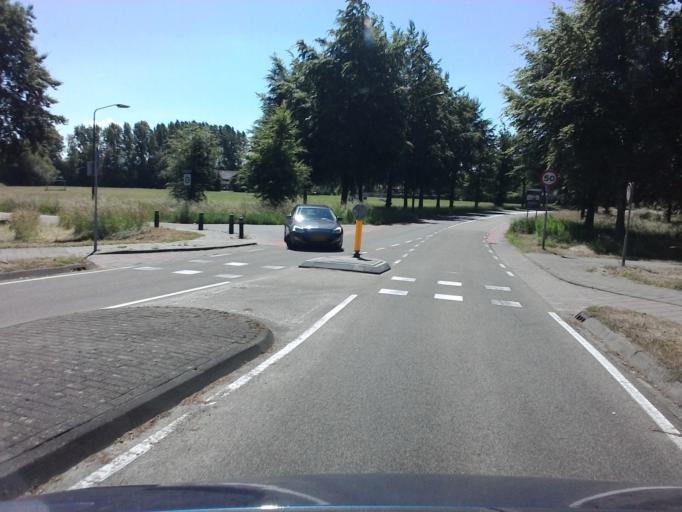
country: NL
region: North Brabant
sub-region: Gemeente Schijndel
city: Schijndel
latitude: 51.6284
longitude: 5.4317
